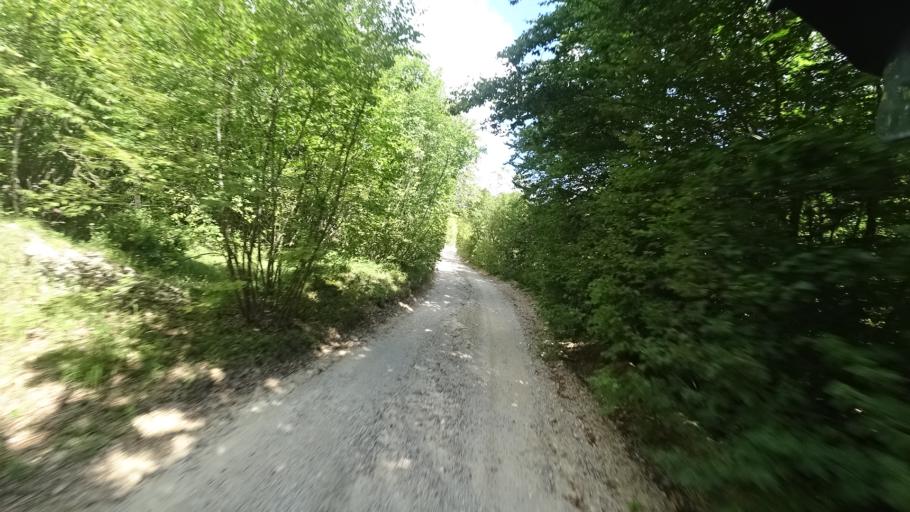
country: HR
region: Zadarska
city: Gracac
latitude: 44.5560
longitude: 15.8255
